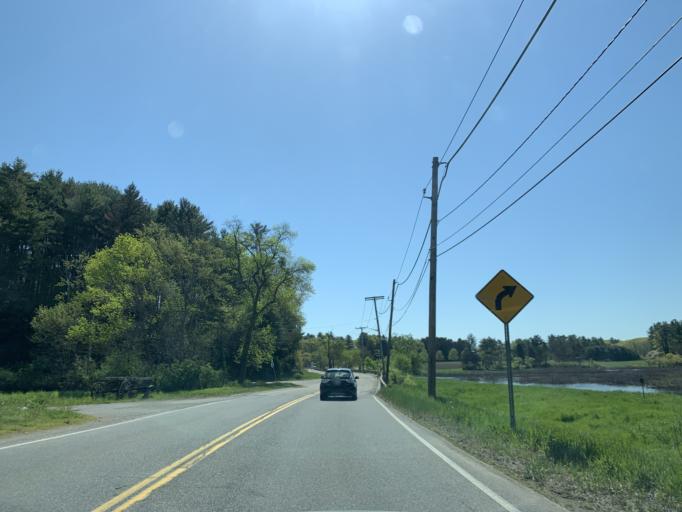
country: US
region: Massachusetts
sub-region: Middlesex County
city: Concord
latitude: 42.4207
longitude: -71.3672
